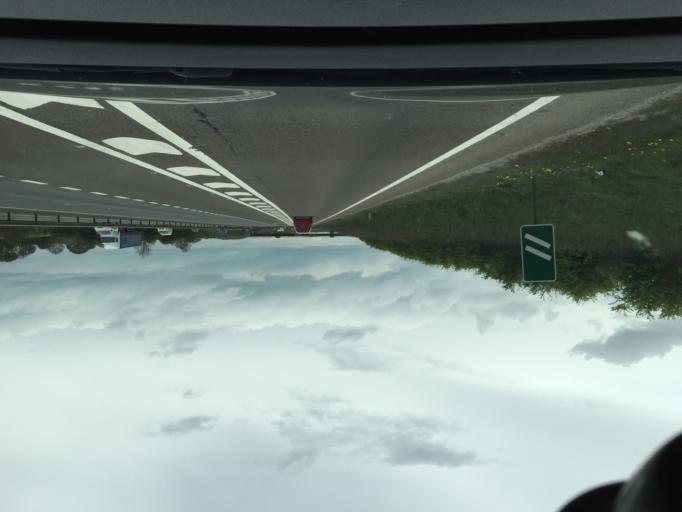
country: GB
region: England
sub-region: West Berkshire
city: Winterbourne
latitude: 51.4428
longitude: -1.3183
